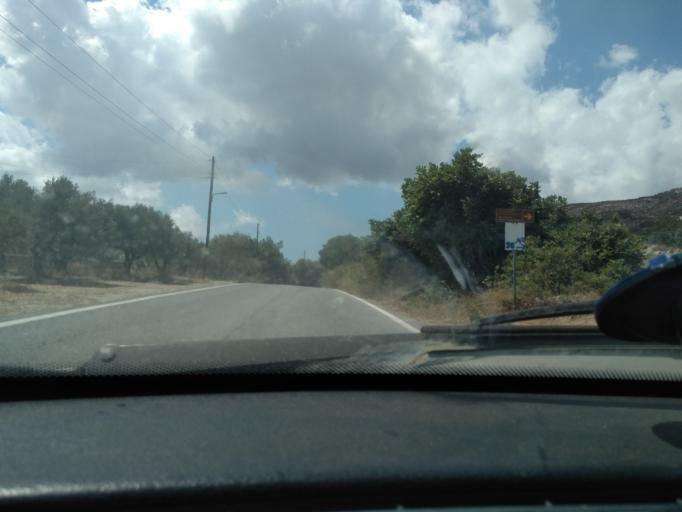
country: GR
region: Crete
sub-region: Nomos Lasithiou
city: Siteia
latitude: 35.1249
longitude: 26.0656
